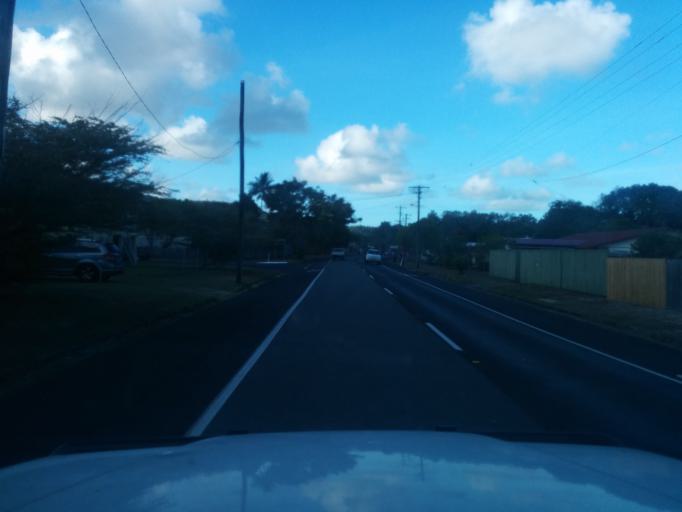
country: AU
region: Queensland
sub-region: Cairns
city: Cairns
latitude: -16.9209
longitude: 145.7466
